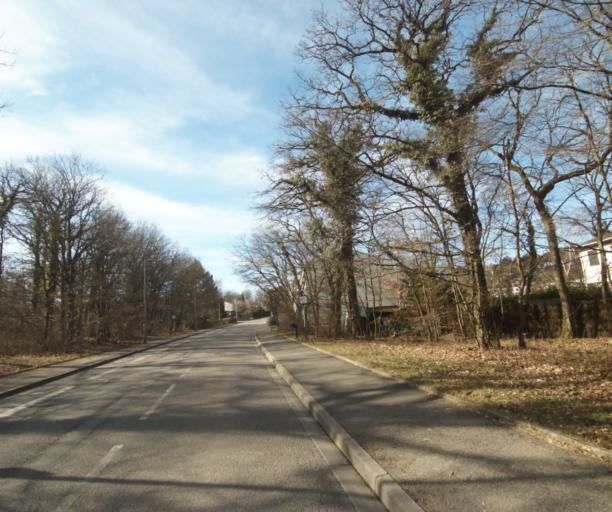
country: FR
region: Lorraine
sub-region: Departement de Meurthe-et-Moselle
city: Villers-les-Nancy
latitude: 48.6504
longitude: 6.1589
